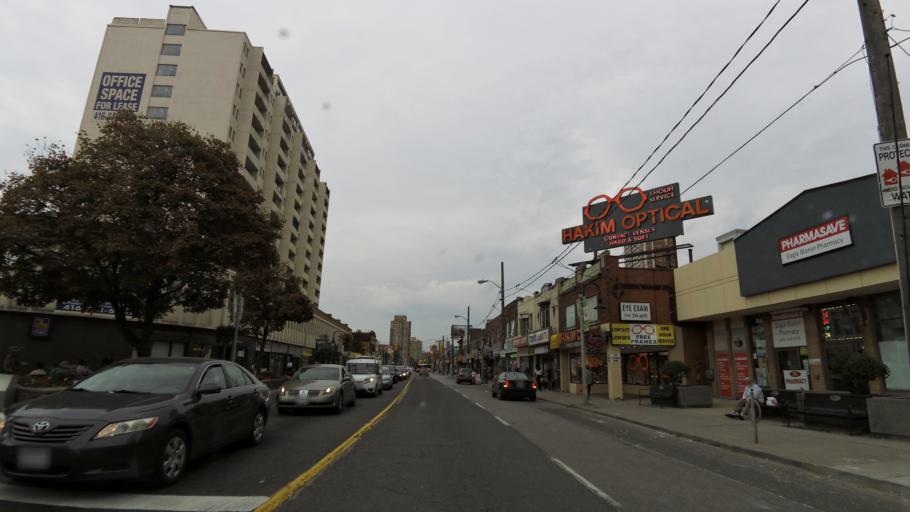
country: CA
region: Ontario
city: Etobicoke
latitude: 43.7002
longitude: -79.5162
